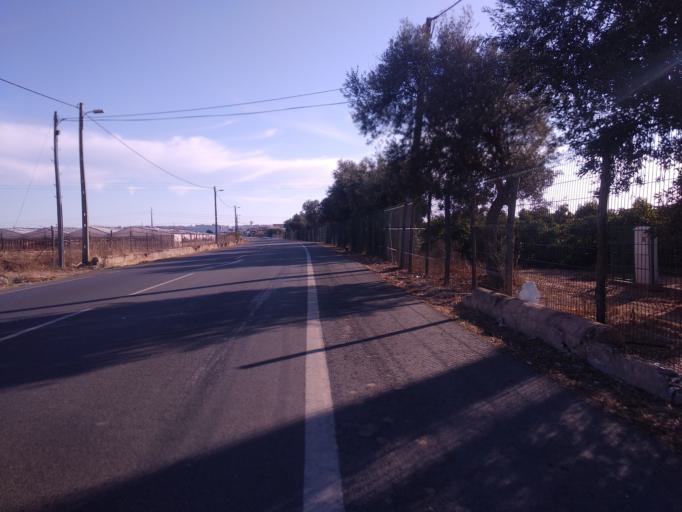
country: PT
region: Faro
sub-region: Faro
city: Faro
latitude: 37.0558
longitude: -7.9257
